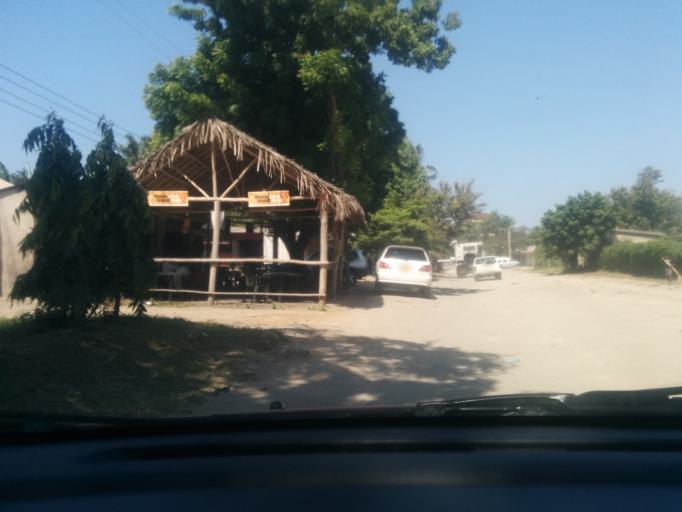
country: TZ
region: Dar es Salaam
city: Magomeni
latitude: -6.7797
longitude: 39.2293
